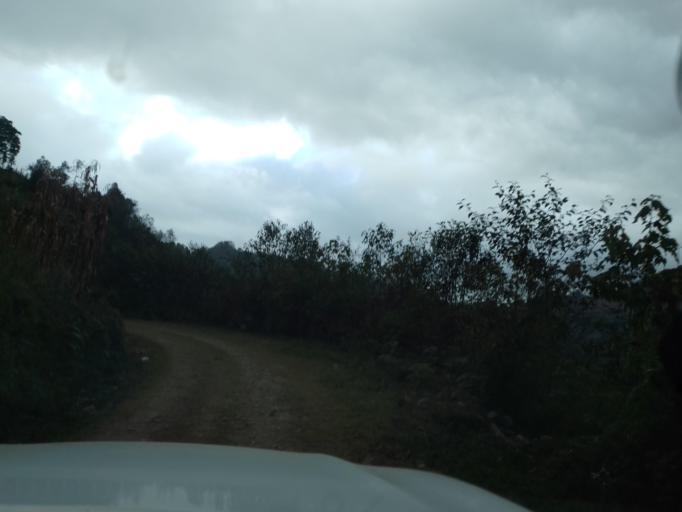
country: GT
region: San Marcos
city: Tacana
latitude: 15.2094
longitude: -92.2174
